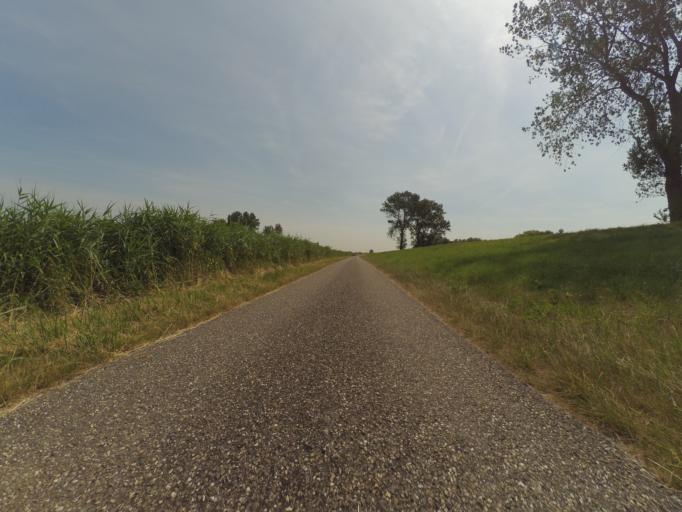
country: NL
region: Zeeland
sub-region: Schouwen-Duiveland
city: Bruinisse
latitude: 51.6322
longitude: 4.1470
